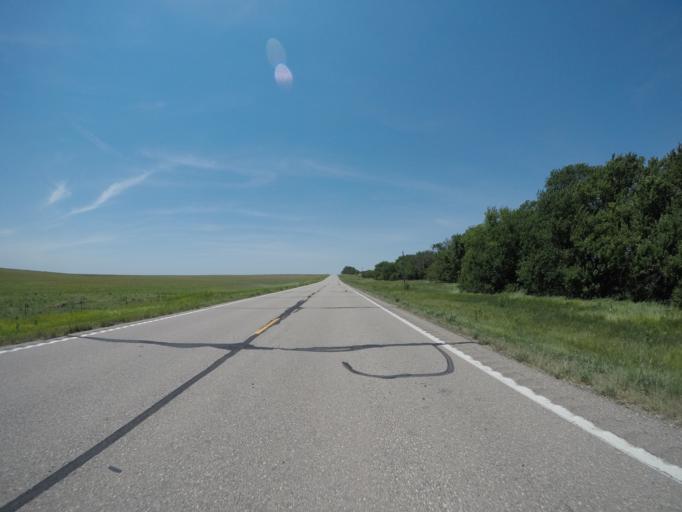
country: US
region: Kansas
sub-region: Dickinson County
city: Solomon
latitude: 39.0306
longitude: -97.3923
